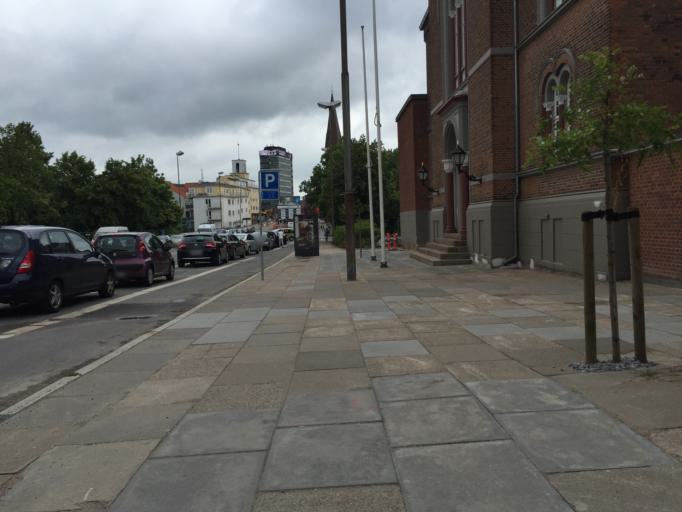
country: DK
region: South Denmark
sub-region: Odense Kommune
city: Odense
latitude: 55.3948
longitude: 10.3935
